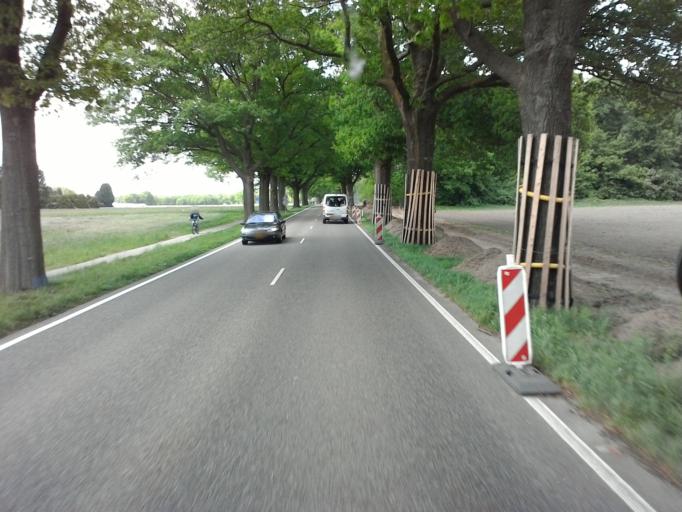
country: NL
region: North Brabant
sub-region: Gemeente Boxmeer
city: Boxmeer
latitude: 51.6493
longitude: 5.9954
